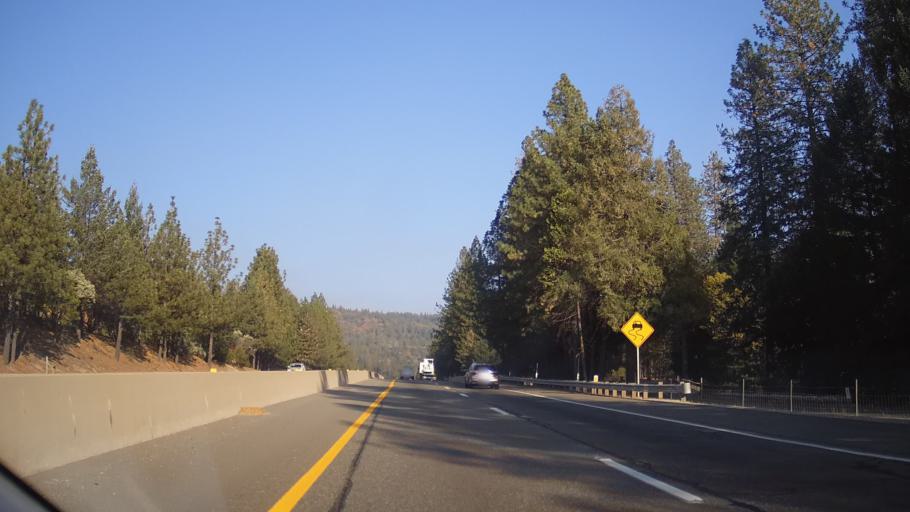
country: US
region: California
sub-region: Placer County
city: Colfax
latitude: 39.1541
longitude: -120.8893
